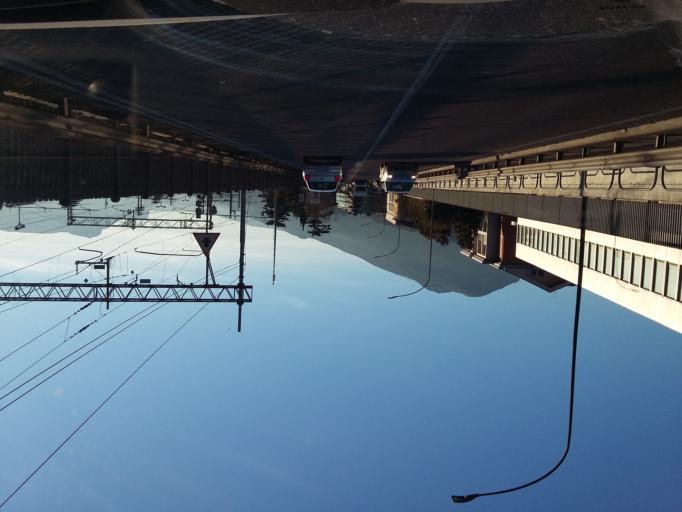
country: IT
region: Trentino-Alto Adige
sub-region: Provincia di Trento
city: Rovereto
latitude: 45.8937
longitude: 11.0356
